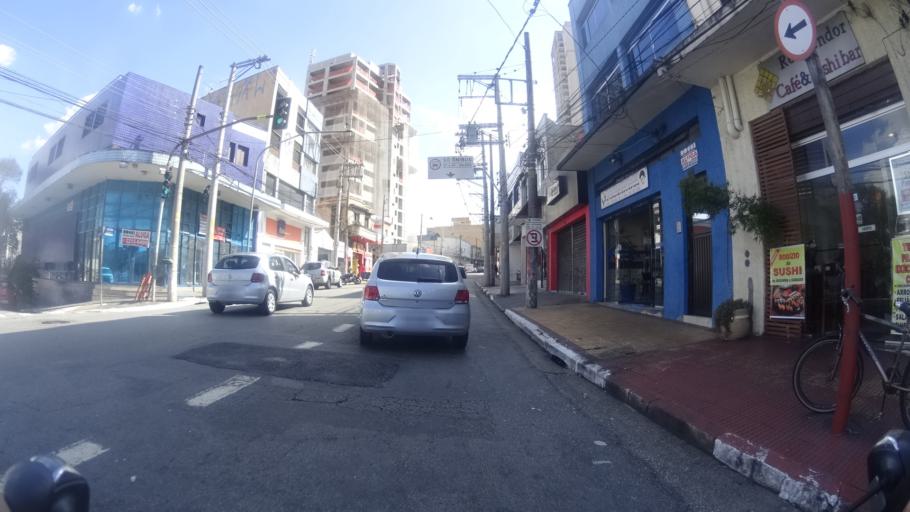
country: BR
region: Sao Paulo
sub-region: Sao Caetano Do Sul
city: Sao Caetano do Sul
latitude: -23.5817
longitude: -46.5872
